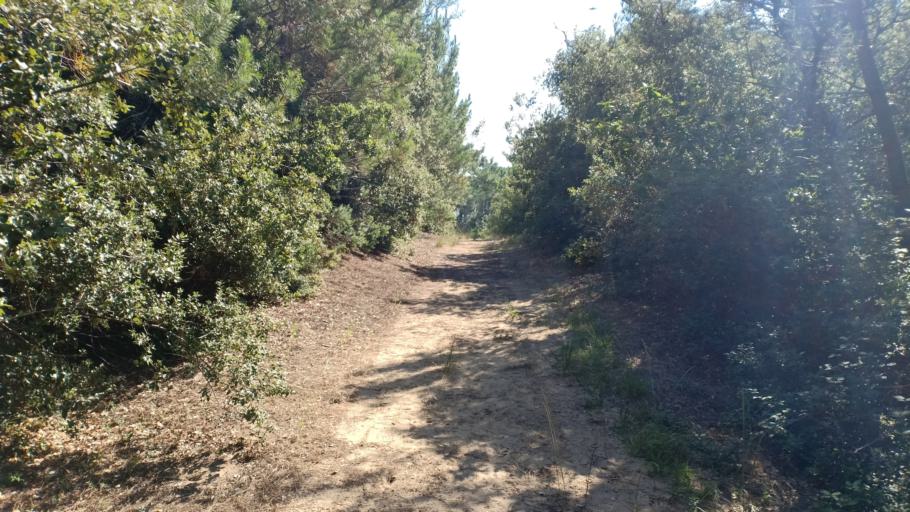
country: FR
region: Poitou-Charentes
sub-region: Departement de la Charente-Maritime
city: Saint-Trojan-les-Bains
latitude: 45.8689
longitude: -1.2489
